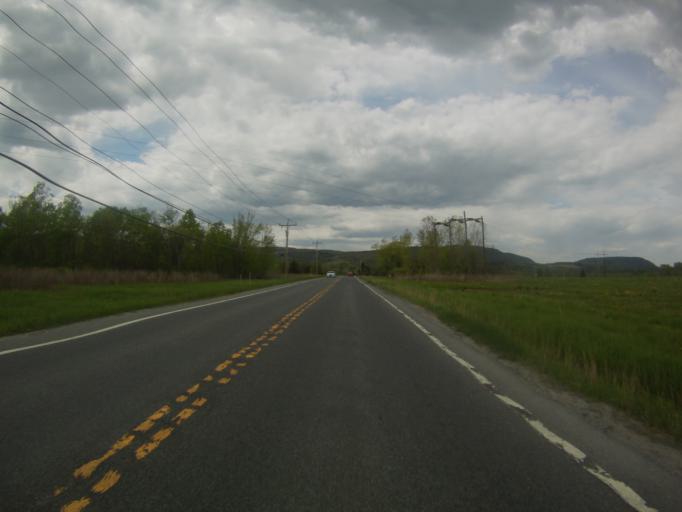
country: US
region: New York
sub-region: Essex County
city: Ticonderoga
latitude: 43.8678
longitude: -73.4394
